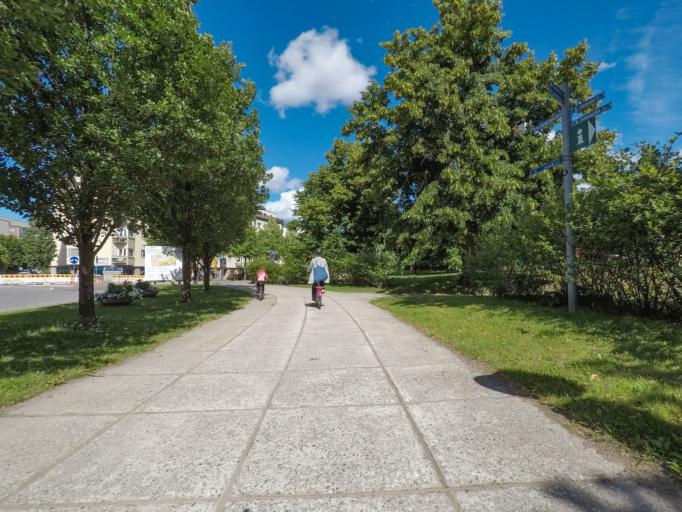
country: FI
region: South Karelia
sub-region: Lappeenranta
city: Lappeenranta
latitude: 61.0593
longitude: 28.1961
